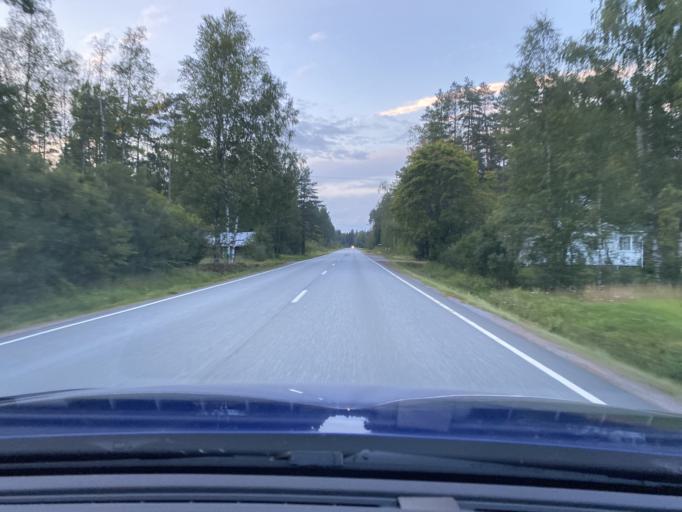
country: FI
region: Satakunta
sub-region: Pohjois-Satakunta
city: Honkajoki
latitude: 62.0466
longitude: 22.2452
